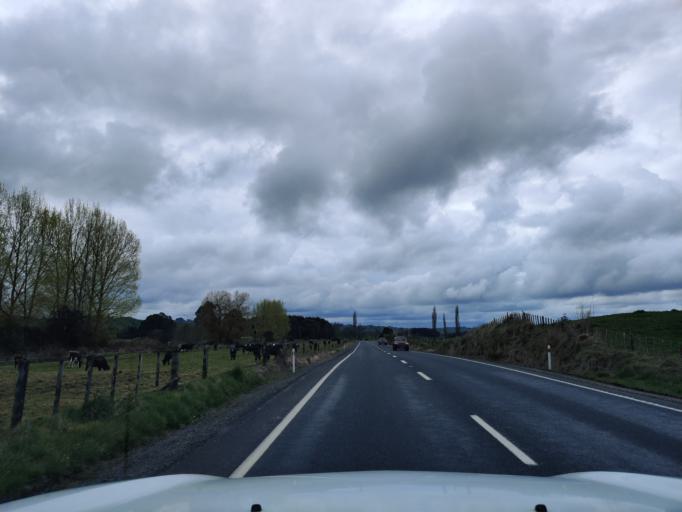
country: NZ
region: Waikato
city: Turangi
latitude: -39.0256
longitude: 175.3817
